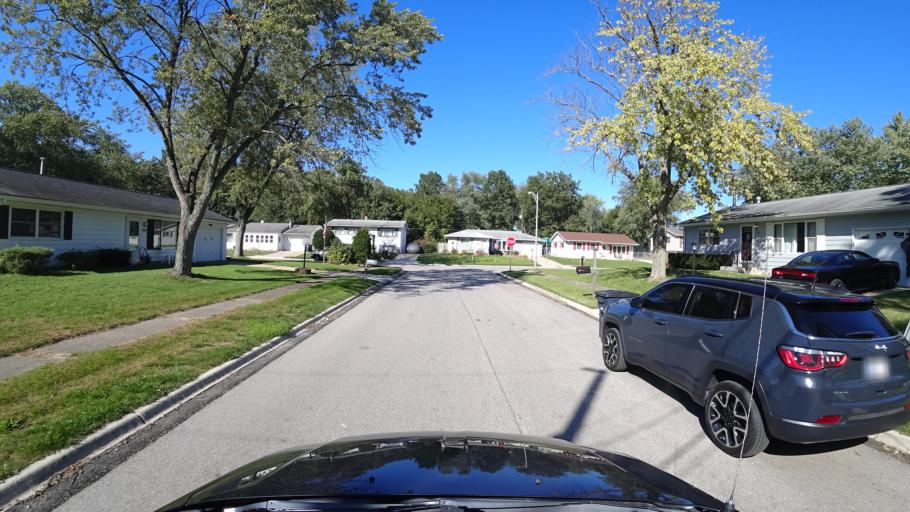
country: US
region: Indiana
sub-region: LaPorte County
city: Michigan City
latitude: 41.6916
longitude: -86.9046
